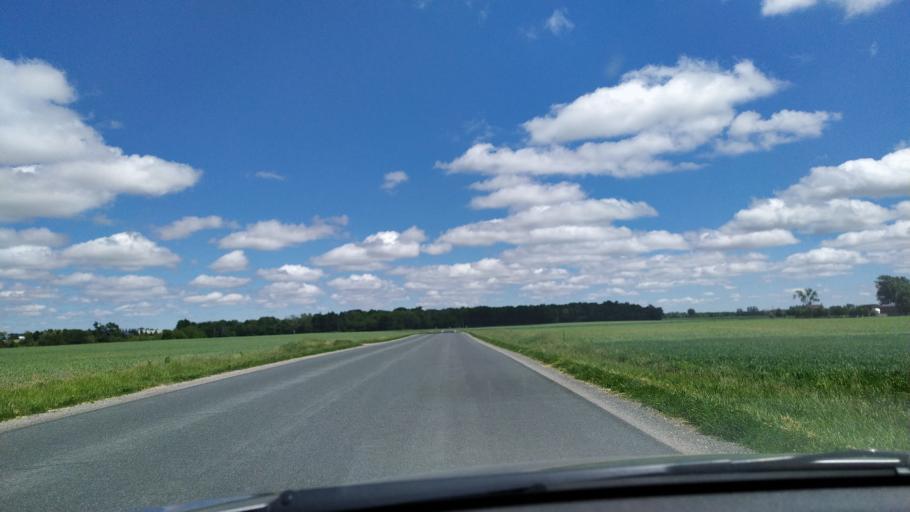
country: CA
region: Ontario
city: Huron East
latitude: 43.4529
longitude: -81.1879
